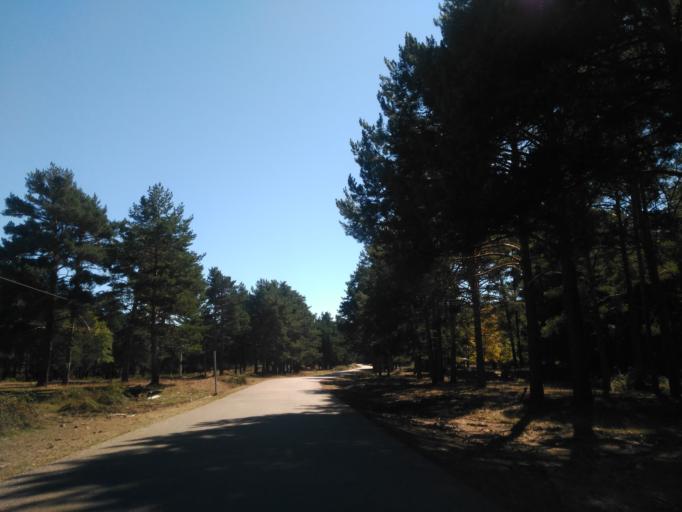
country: ES
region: Castille and Leon
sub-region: Provincia de Soria
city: Vinuesa
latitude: 41.9537
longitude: -2.7818
